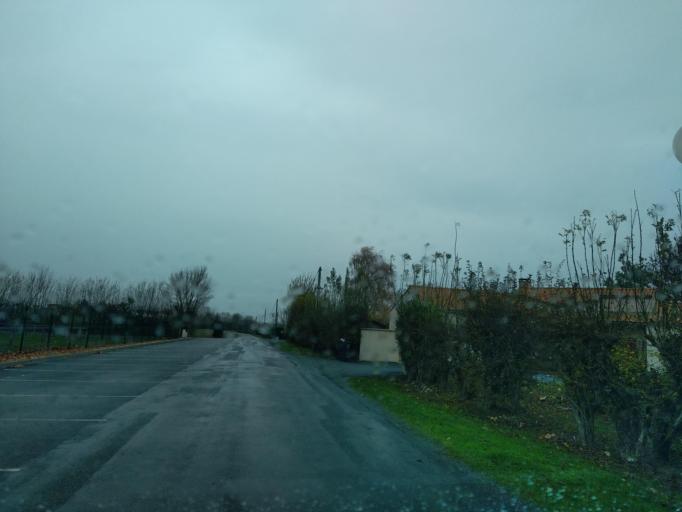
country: FR
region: Pays de la Loire
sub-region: Departement de la Vendee
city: Maillezais
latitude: 46.3697
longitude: -0.7353
